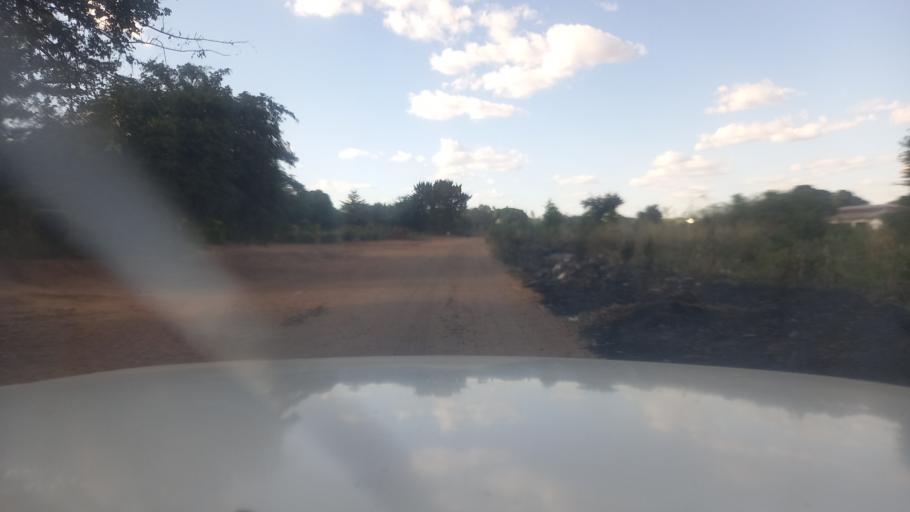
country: ZM
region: Southern
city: Livingstone
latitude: -17.8295
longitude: 25.8680
